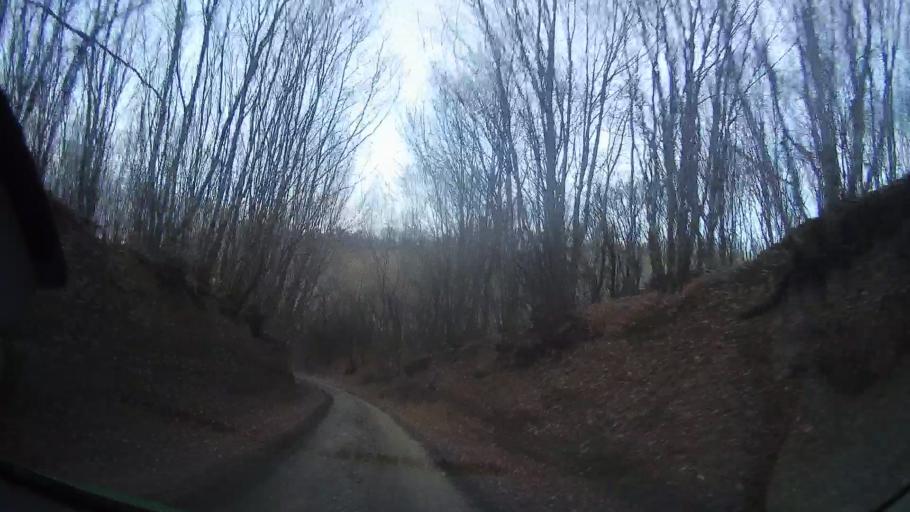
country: RO
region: Cluj
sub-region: Comuna Palatca
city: Palatca
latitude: 46.8611
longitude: 24.0257
